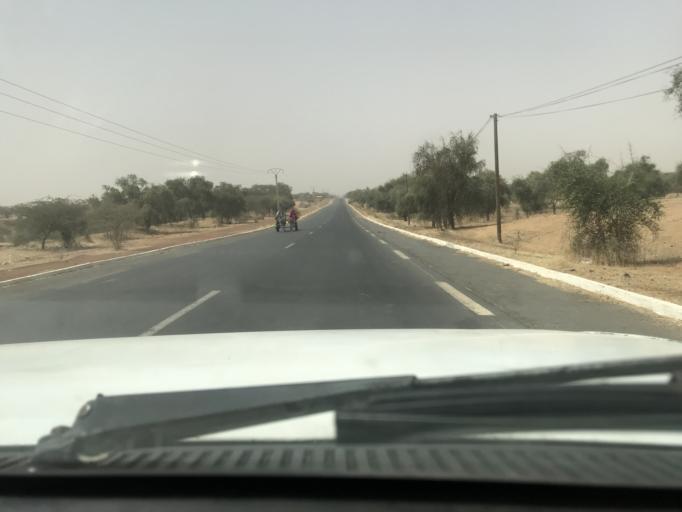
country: SN
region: Louga
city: Ndibene Dahra
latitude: 15.3468
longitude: -15.4496
